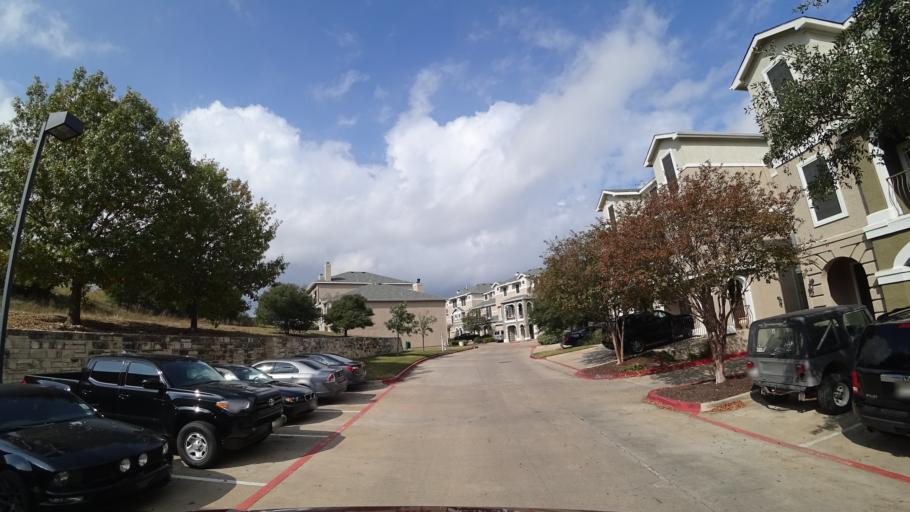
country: US
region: Texas
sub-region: Travis County
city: Hudson Bend
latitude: 30.3844
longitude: -97.8795
